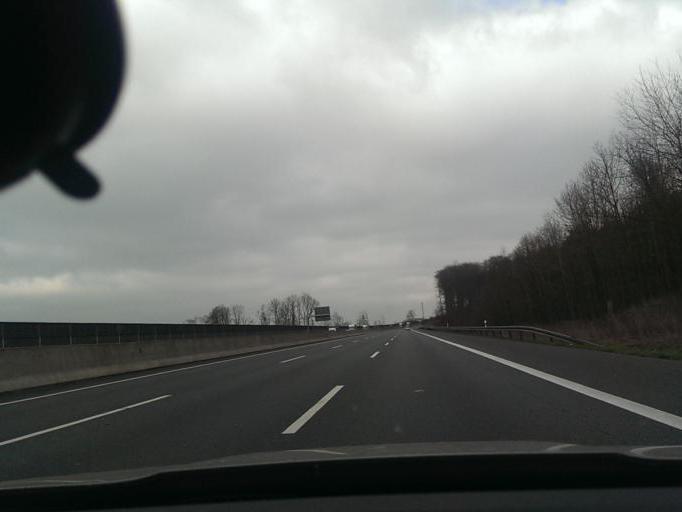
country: DE
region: Lower Saxony
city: Buchholz
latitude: 52.2196
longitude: 9.1413
